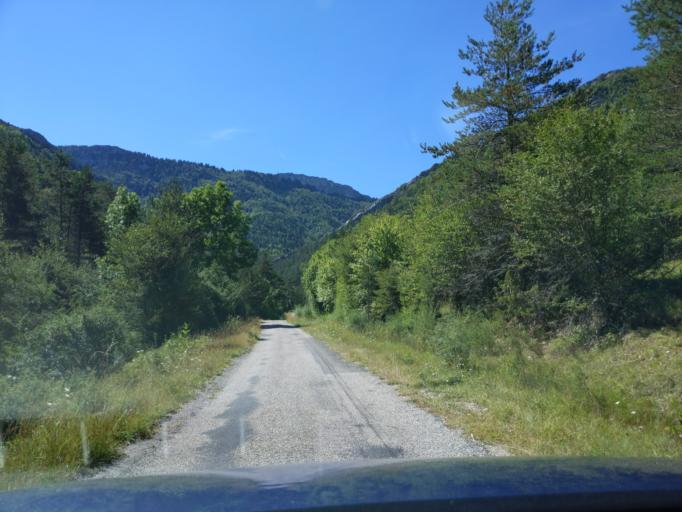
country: FR
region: Rhone-Alpes
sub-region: Departement de la Drome
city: Die
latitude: 44.6295
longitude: 5.5544
